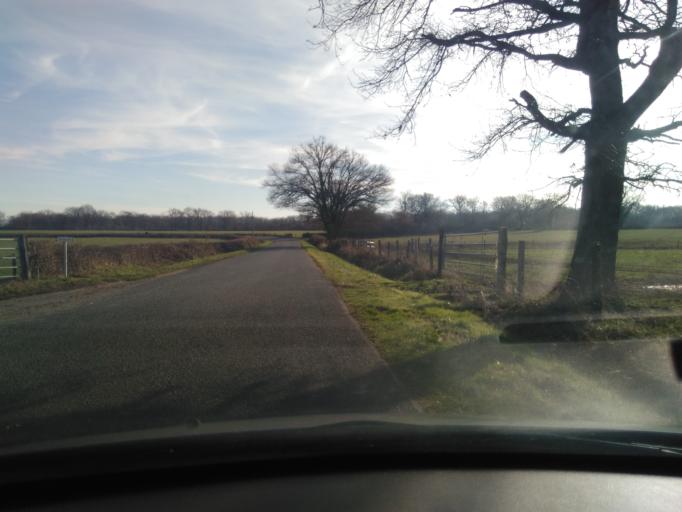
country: FR
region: Centre
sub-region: Departement du Cher
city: Orval
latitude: 46.6507
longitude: 2.4452
